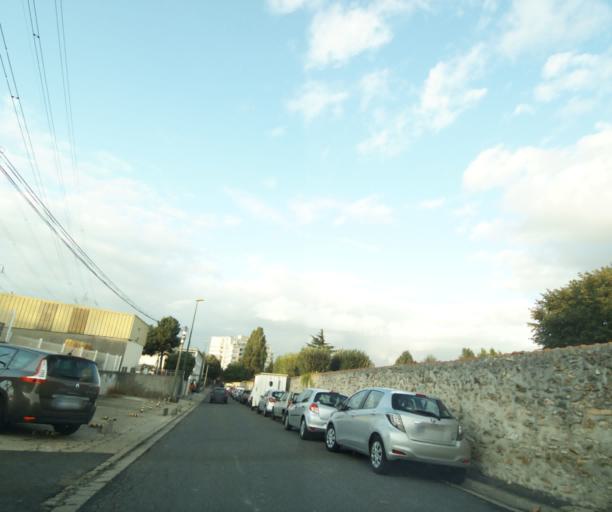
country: FR
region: Ile-de-France
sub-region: Departement des Hauts-de-Seine
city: Le Plessis-Robinson
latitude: 48.7829
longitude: 2.2488
